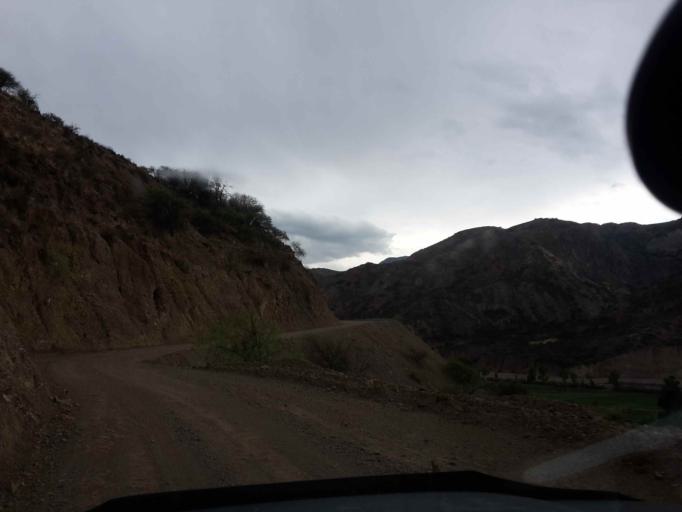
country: BO
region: Cochabamba
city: Sipe Sipe
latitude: -17.5273
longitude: -66.5284
